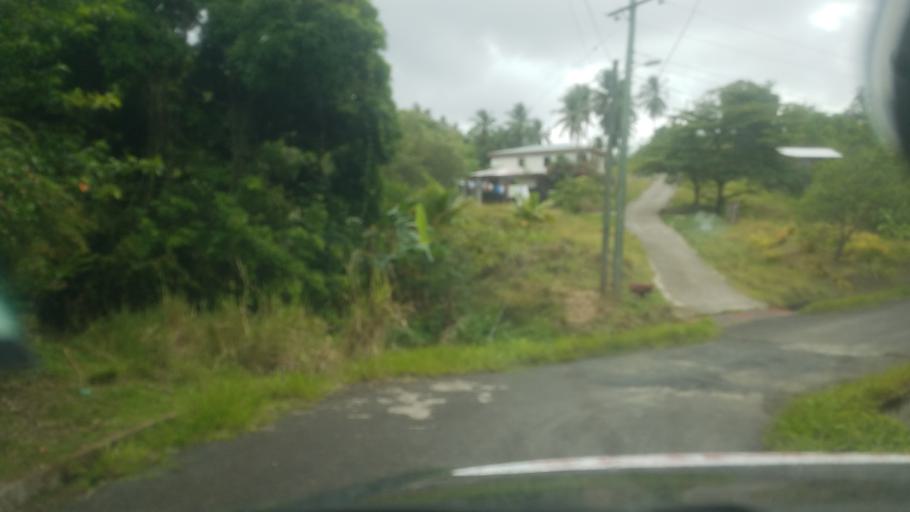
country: LC
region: Laborie Quarter
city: Laborie
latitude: 13.7640
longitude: -60.9743
